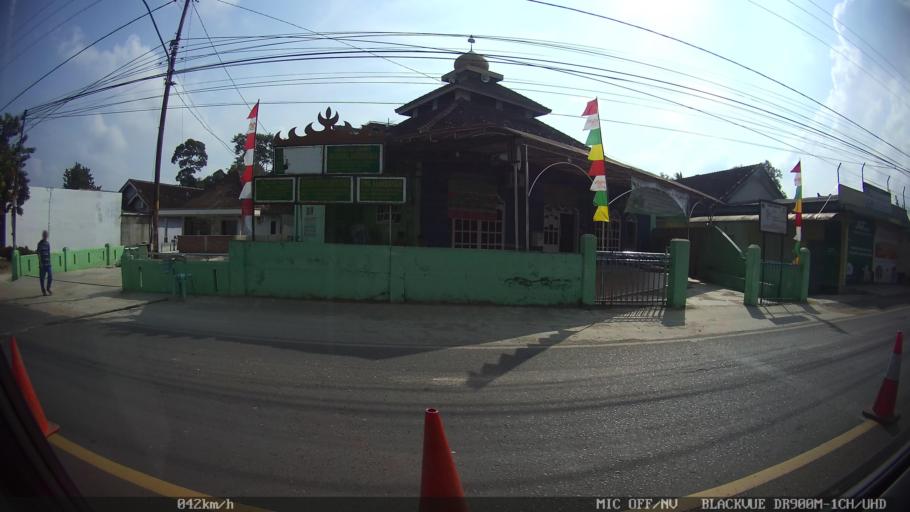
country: ID
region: Lampung
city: Kedaton
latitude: -5.3832
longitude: 105.1997
